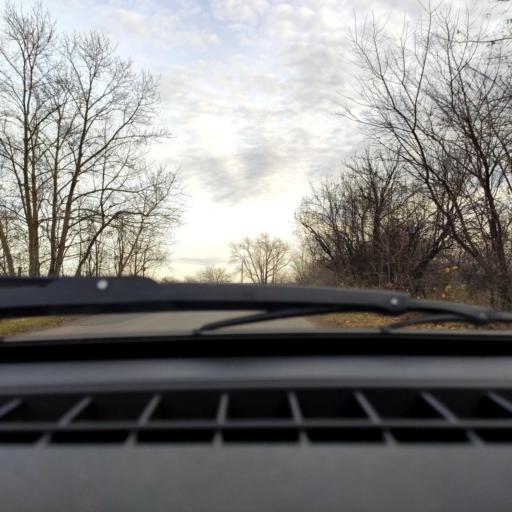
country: RU
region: Bashkortostan
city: Ufa
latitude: 54.8735
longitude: 56.1306
